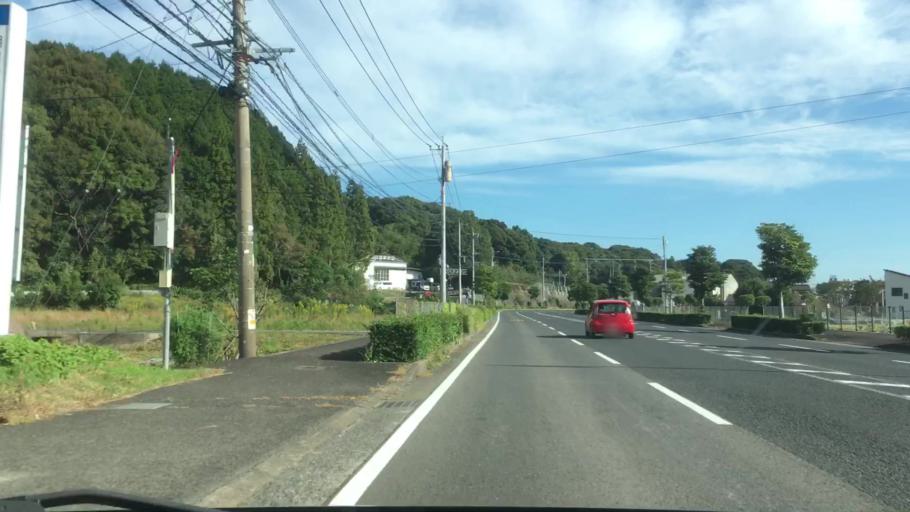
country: JP
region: Nagasaki
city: Sasebo
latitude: 33.1116
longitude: 129.7867
